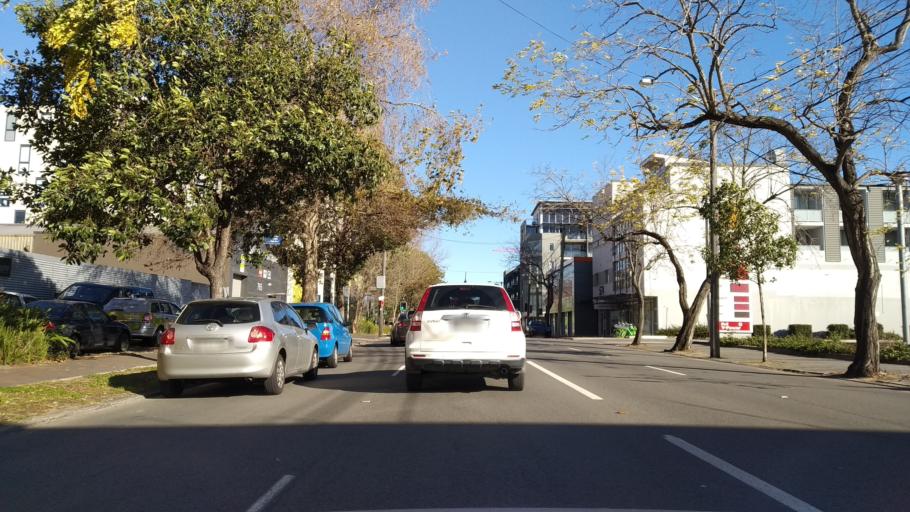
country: AU
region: New South Wales
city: Alexandria
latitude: -33.9173
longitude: 151.1998
